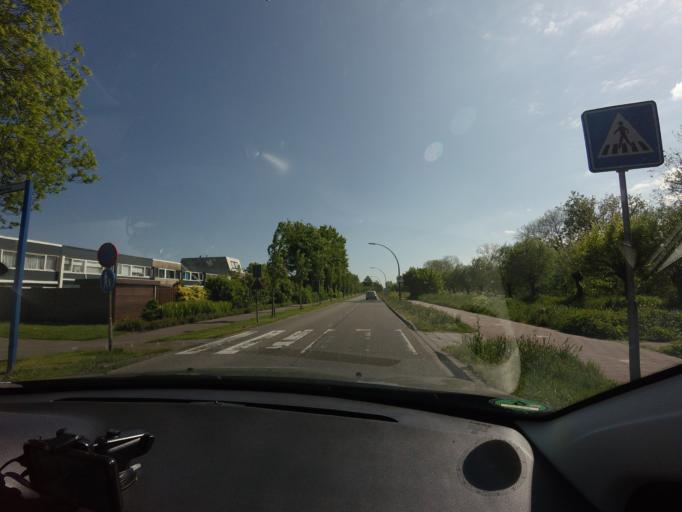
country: NL
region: Utrecht
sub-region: Gemeente De Ronde Venen
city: Mijdrecht
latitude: 52.2101
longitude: 4.9198
